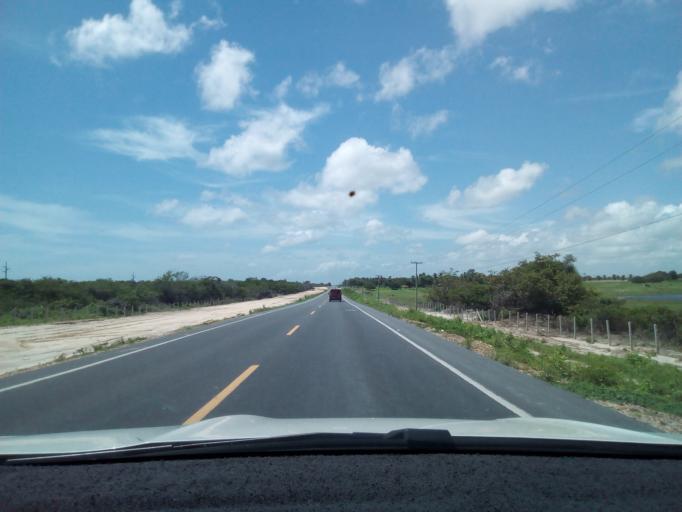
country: BR
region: Ceara
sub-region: Beberibe
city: Beberibe
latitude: -4.2870
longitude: -38.0254
